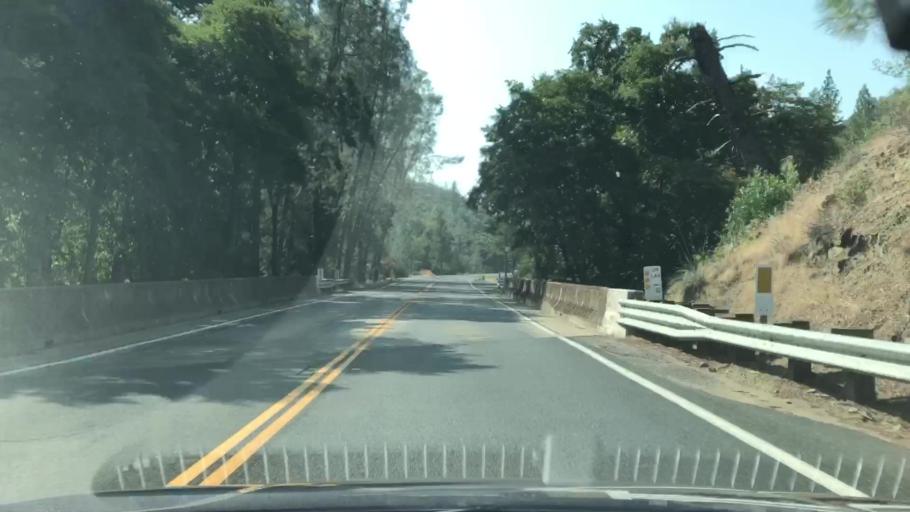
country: US
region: California
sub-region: Lake County
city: Middletown
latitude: 38.6957
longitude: -122.5990
